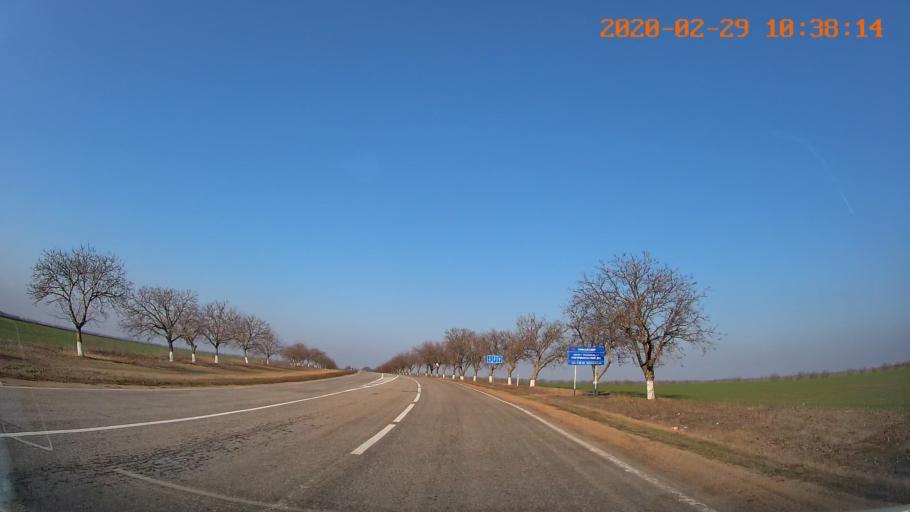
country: MD
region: Anenii Noi
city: Varnita
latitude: 47.0146
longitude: 29.4769
